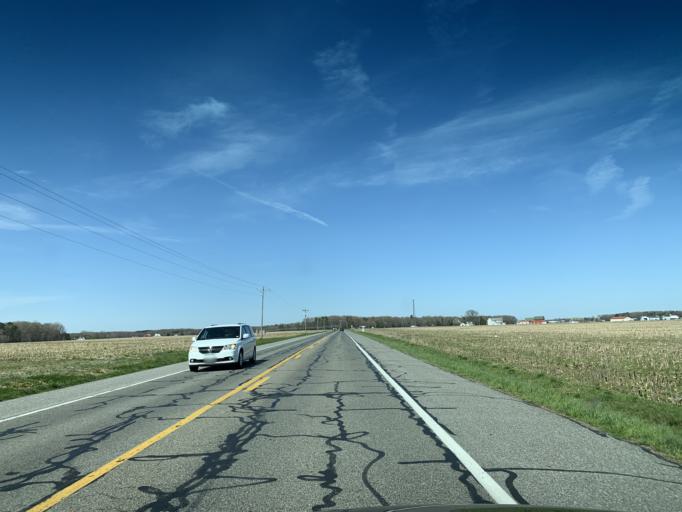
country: US
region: Delaware
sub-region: Kent County
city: Harrington
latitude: 38.9124
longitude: -75.6041
